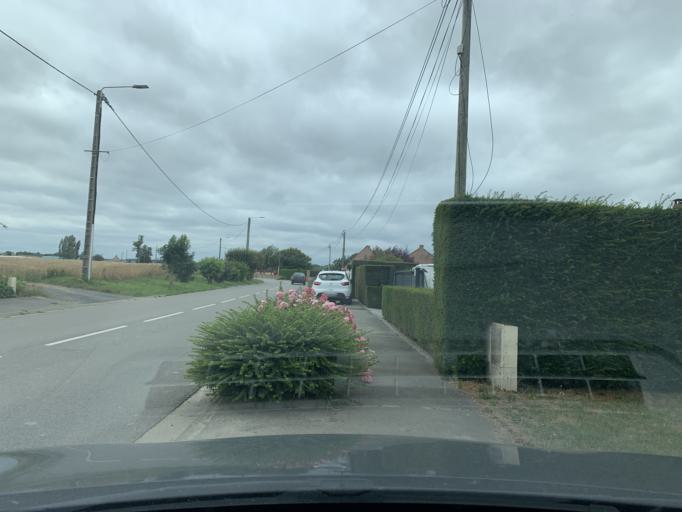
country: FR
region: Nord-Pas-de-Calais
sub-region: Departement du Nord
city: Fechain
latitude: 50.2551
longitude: 3.1901
